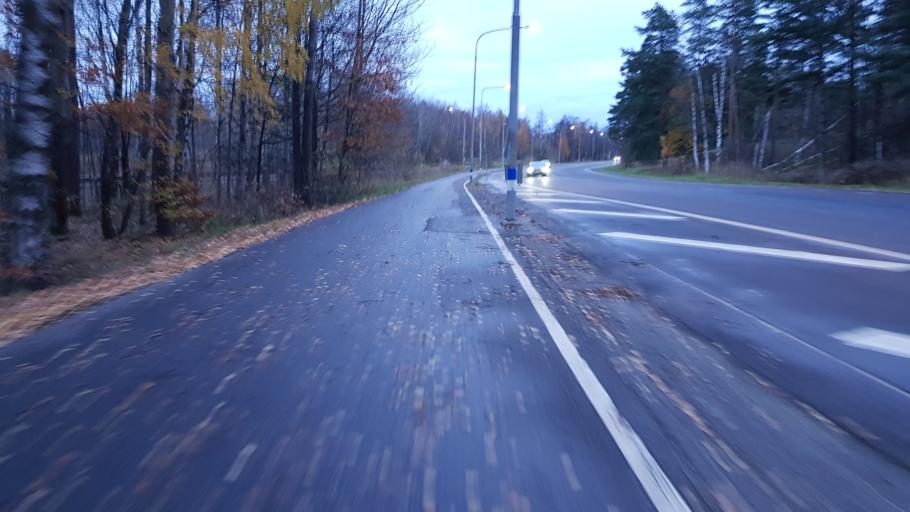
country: SE
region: OEstergoetland
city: Lindo
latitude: 58.5964
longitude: 16.2337
